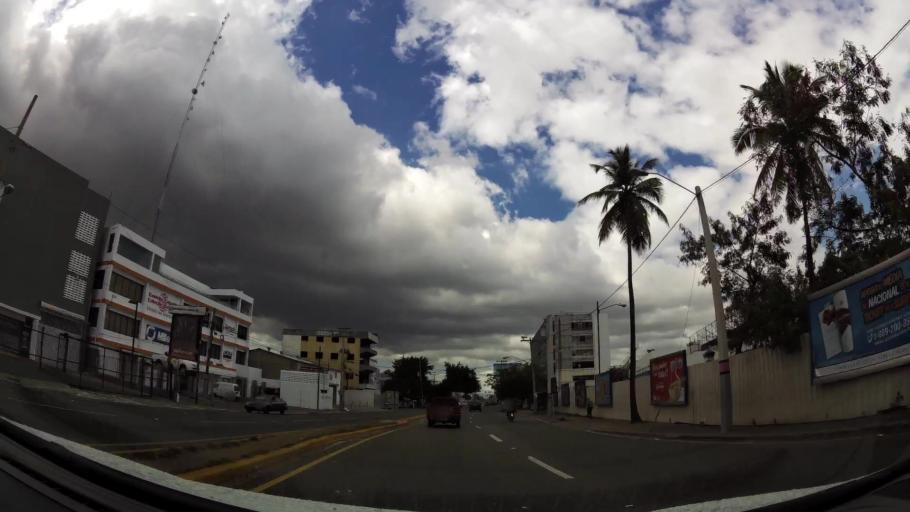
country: DO
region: Nacional
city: San Carlos
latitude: 18.4829
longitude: -69.9142
